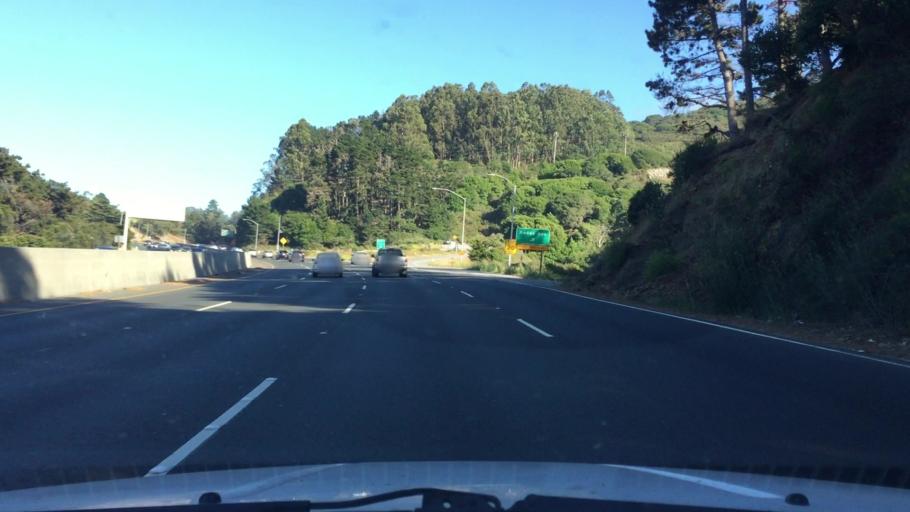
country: US
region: California
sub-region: Marin County
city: Marin City
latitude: 37.8621
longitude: -122.5054
